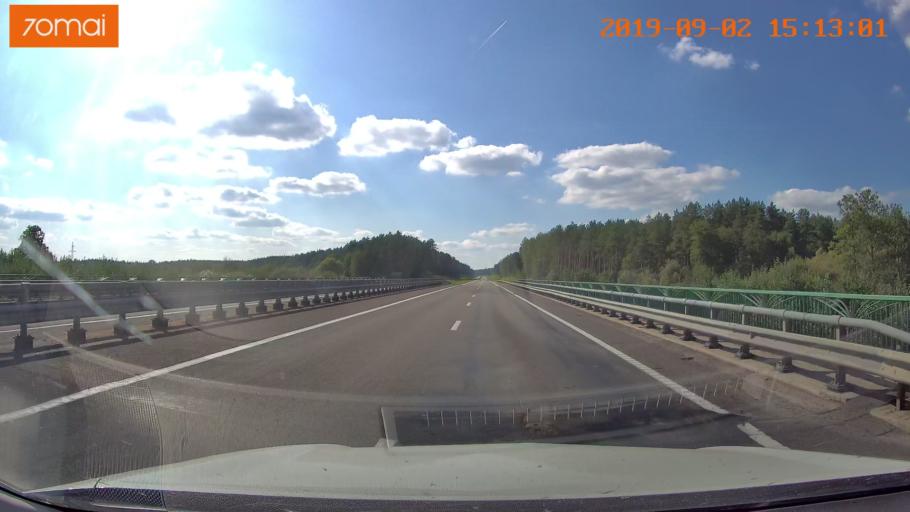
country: BY
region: Mogilev
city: Byalynichy
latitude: 53.9672
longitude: 29.7136
